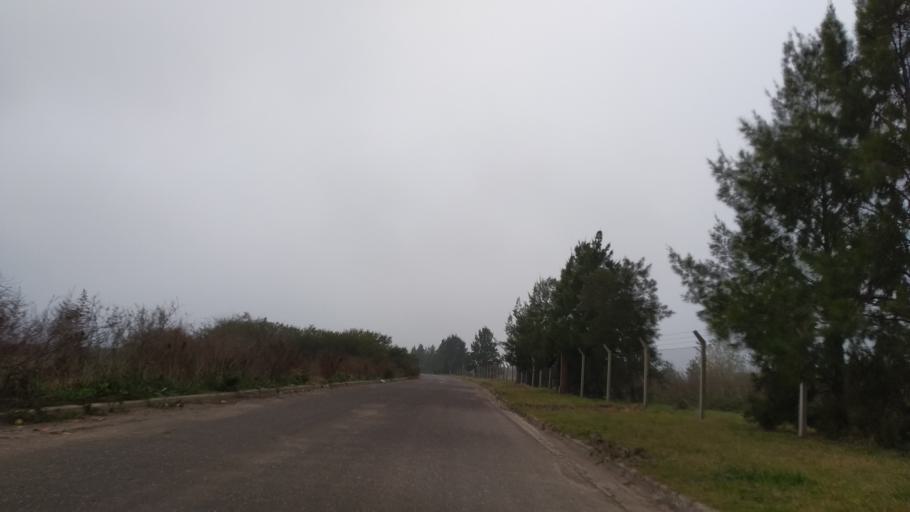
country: AR
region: Santa Fe
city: Funes
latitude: -32.9387
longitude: -60.7701
